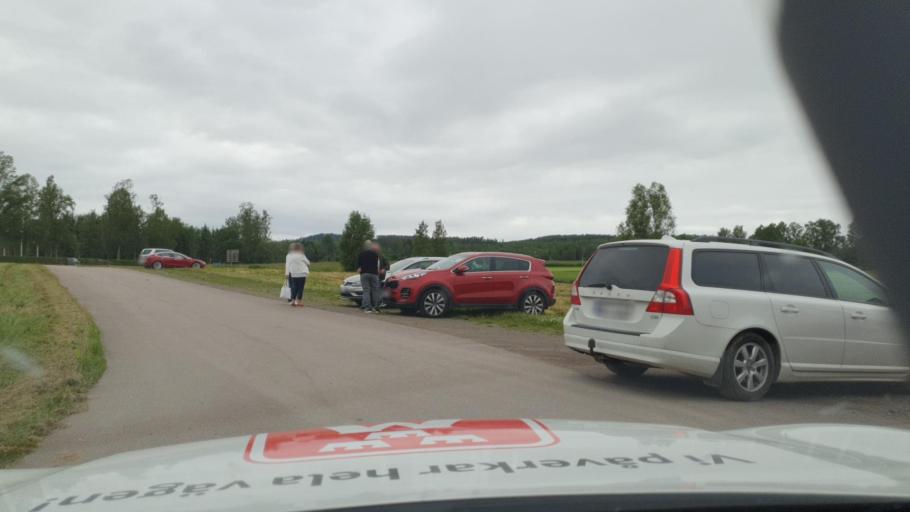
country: SE
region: Vaermland
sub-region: Sunne Kommun
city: Sunne
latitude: 59.8021
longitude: 13.1265
